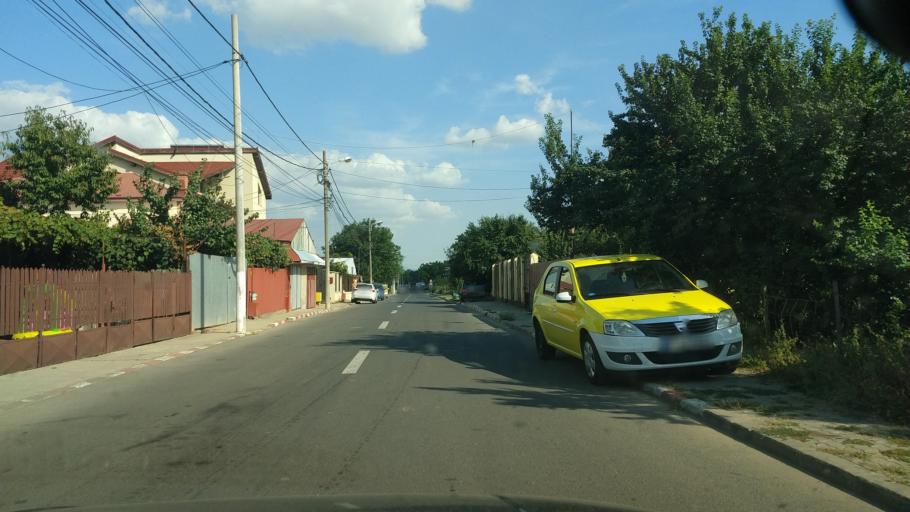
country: RO
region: Ilfov
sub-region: Voluntari City
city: Voluntari
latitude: 44.4934
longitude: 26.1613
